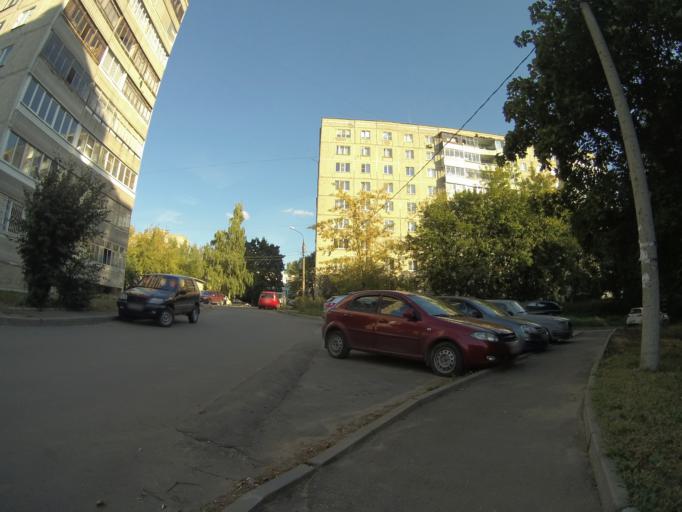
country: RU
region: Vladimir
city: Vladimir
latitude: 56.1507
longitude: 40.3661
